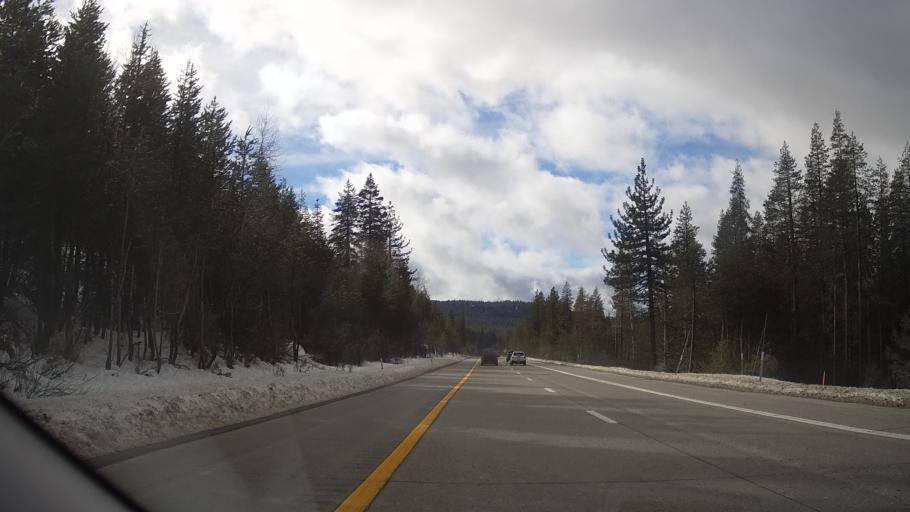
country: US
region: California
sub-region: Nevada County
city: Truckee
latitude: 39.3213
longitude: -120.4233
